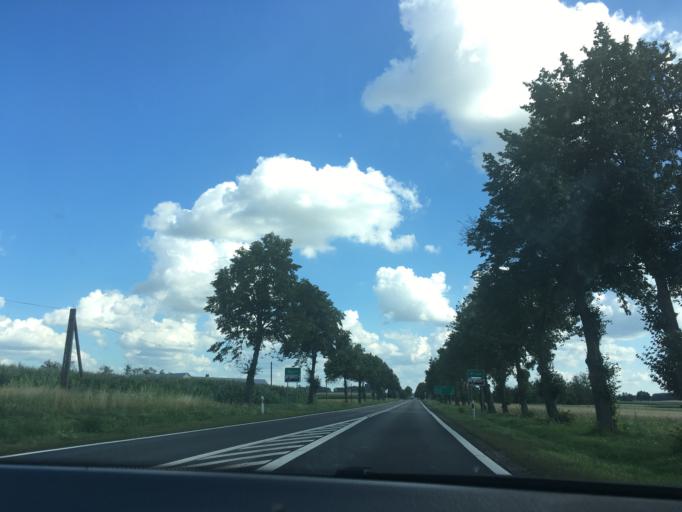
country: PL
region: Podlasie
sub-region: Powiat sokolski
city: Janow
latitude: 53.4390
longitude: 23.0962
